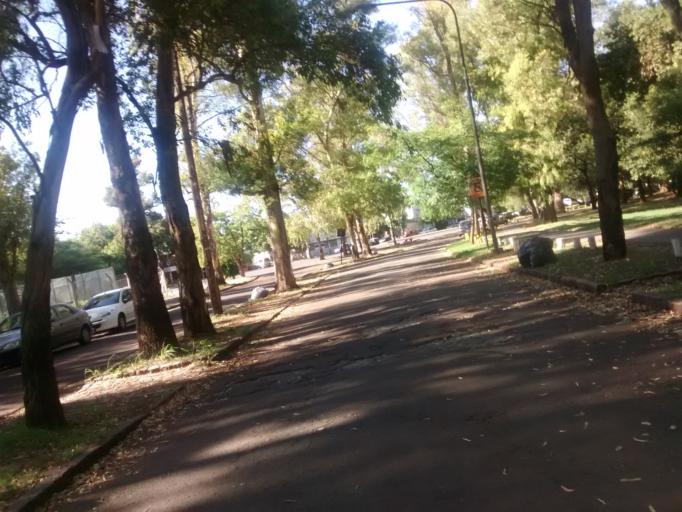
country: AR
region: Buenos Aires
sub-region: Partido de La Plata
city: La Plata
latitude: -34.9124
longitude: -57.9334
